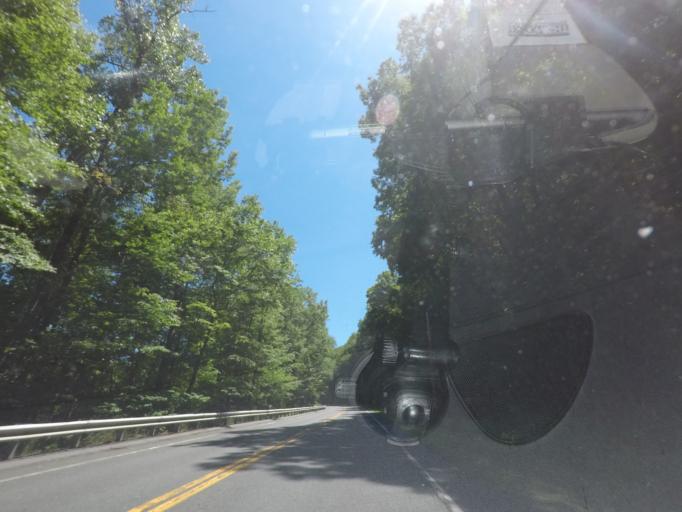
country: US
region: Massachusetts
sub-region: Hampshire County
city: Westhampton
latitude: 42.2504
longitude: -72.9311
